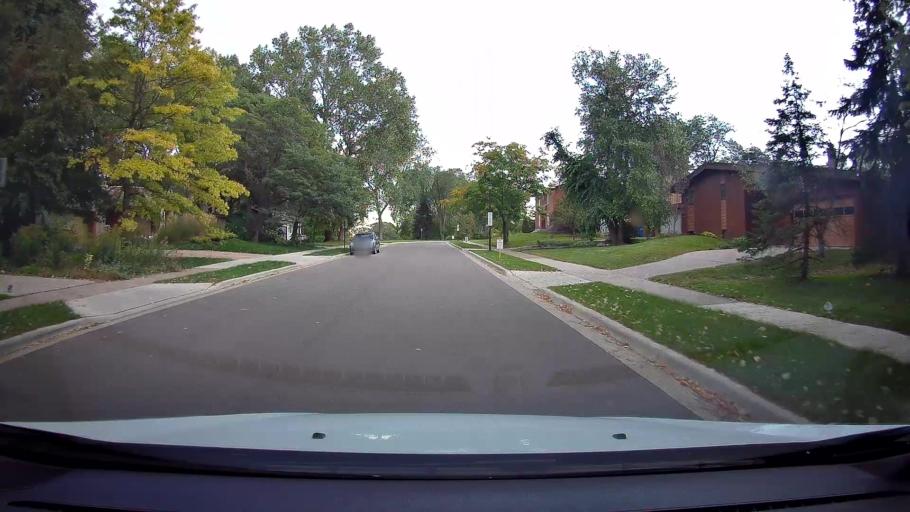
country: US
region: Minnesota
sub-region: Ramsey County
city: Lauderdale
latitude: 44.9889
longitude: -93.1898
